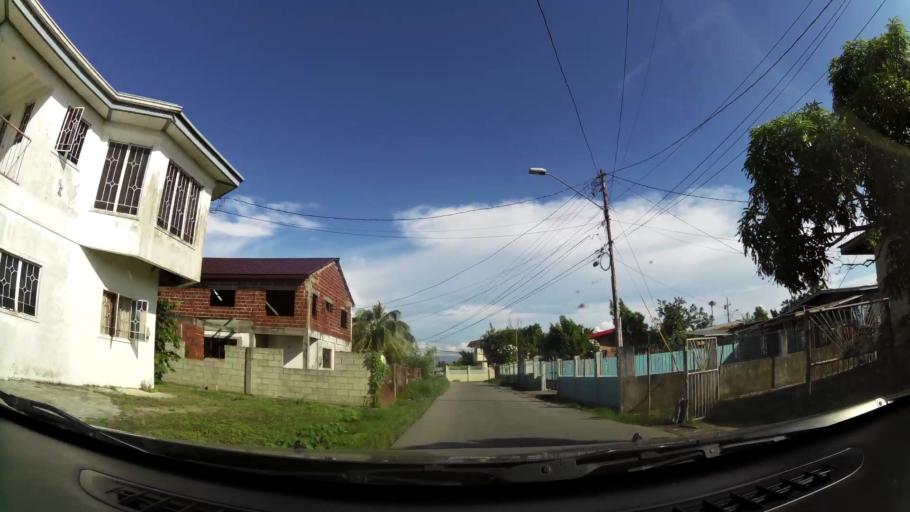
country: TT
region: Chaguanas
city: Chaguanas
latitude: 10.5256
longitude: -61.3904
